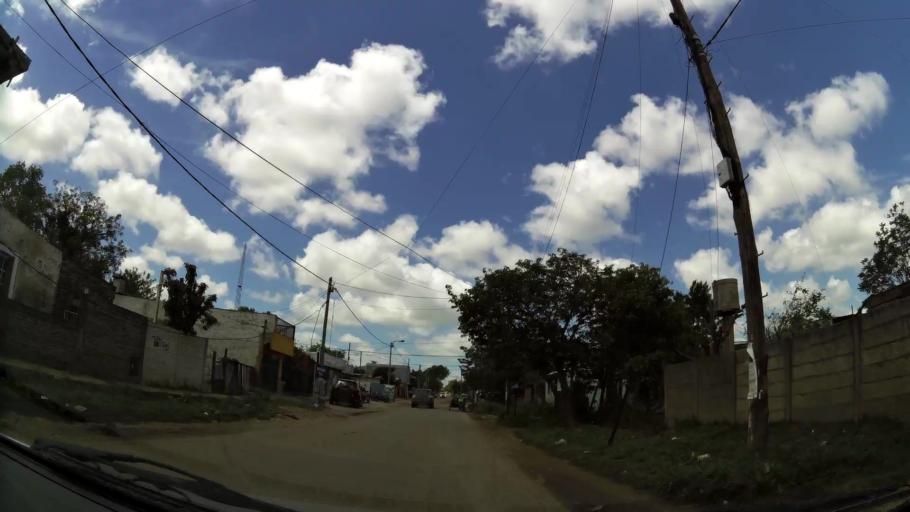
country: AR
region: Buenos Aires
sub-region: Partido de Quilmes
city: Quilmes
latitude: -34.8208
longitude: -58.2370
